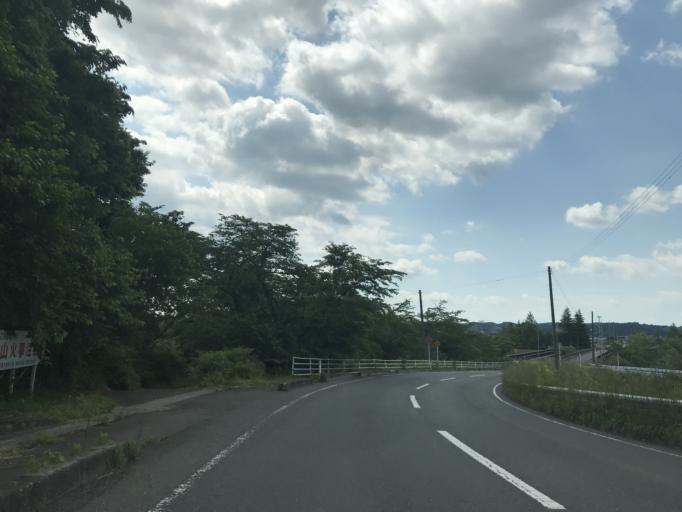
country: JP
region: Miyagi
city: Furukawa
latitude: 38.7480
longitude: 140.9534
